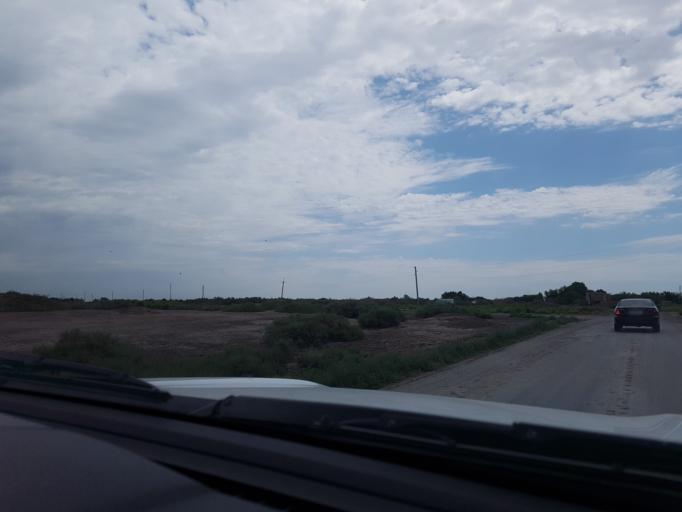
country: TM
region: Dasoguz
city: Koeneuergench
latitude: 42.2943
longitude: 59.1437
